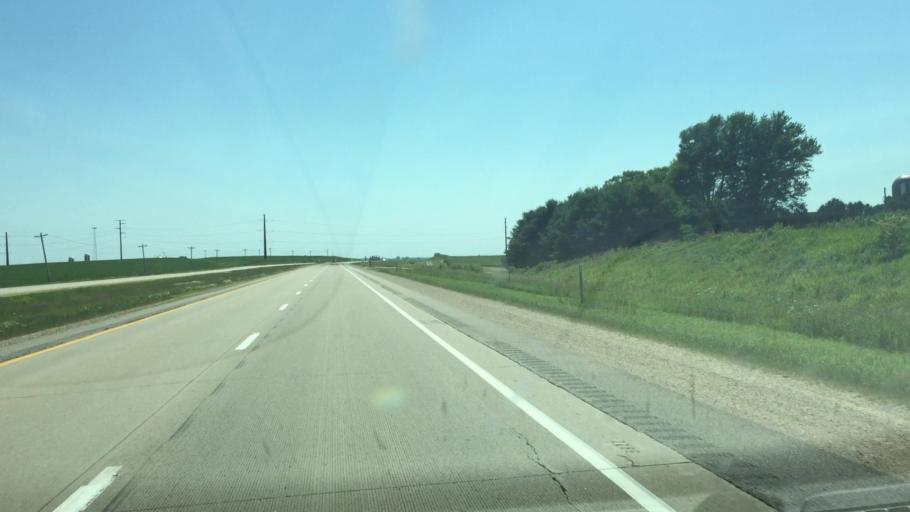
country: US
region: Iowa
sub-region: Dubuque County
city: Peosta
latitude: 42.3679
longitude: -90.7954
